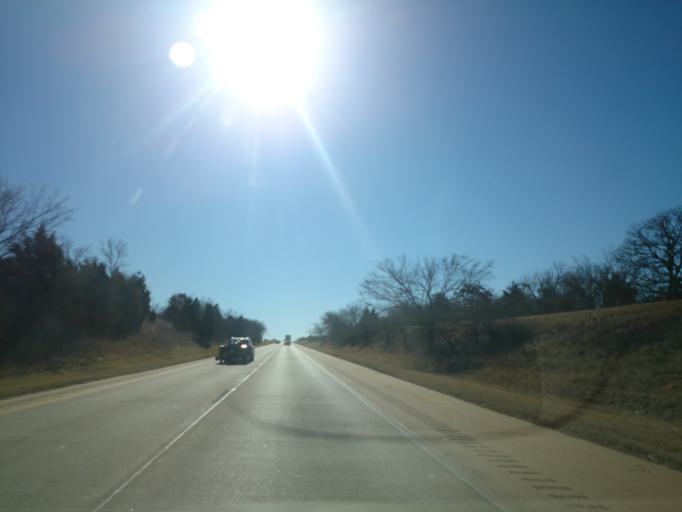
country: US
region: Oklahoma
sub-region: Logan County
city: Guthrie
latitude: 35.7744
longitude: -97.4164
